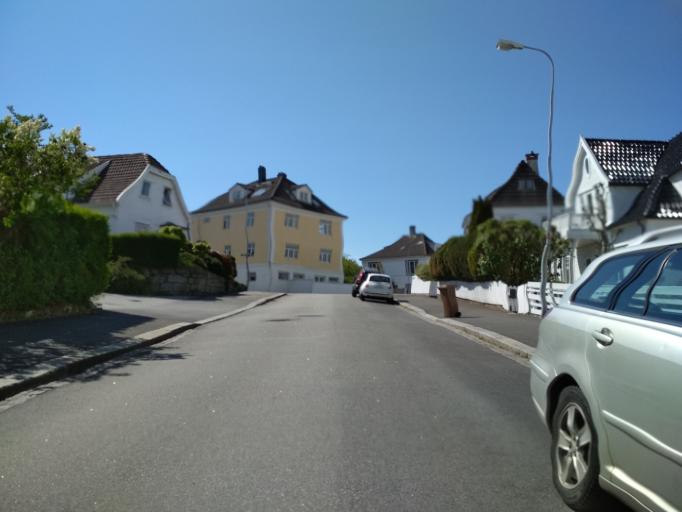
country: NO
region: Rogaland
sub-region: Stavanger
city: Stavanger
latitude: 58.9588
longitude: 5.7312
